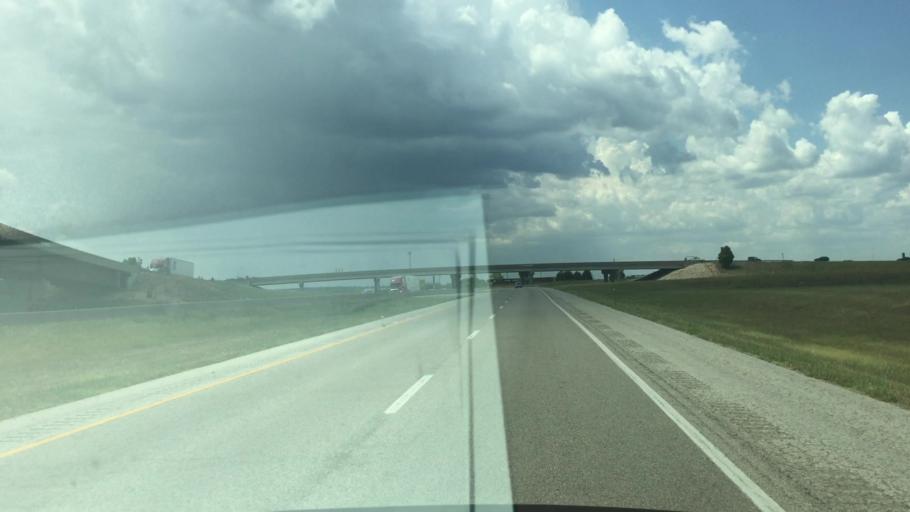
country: US
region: Kansas
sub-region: Shawnee County
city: Topeka
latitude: 39.0312
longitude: -95.6103
